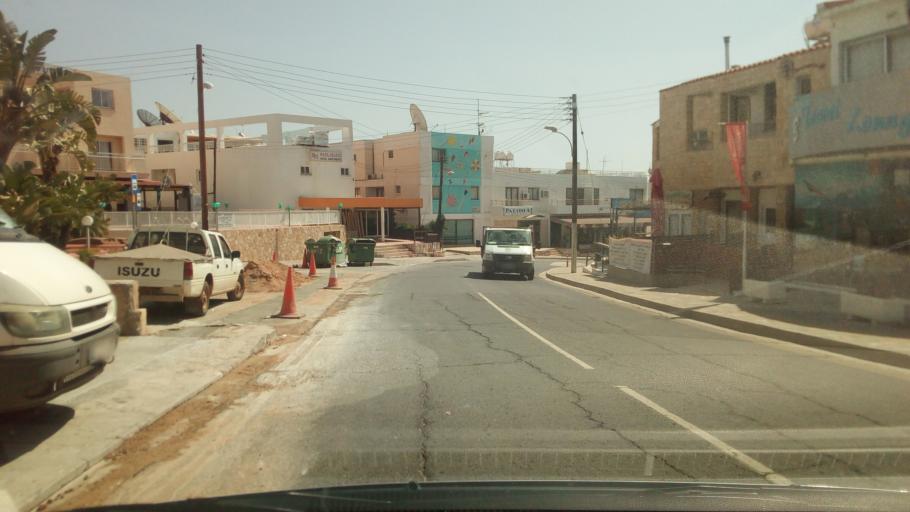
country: CY
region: Ammochostos
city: Ayia Napa
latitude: 34.9927
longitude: 34.0004
